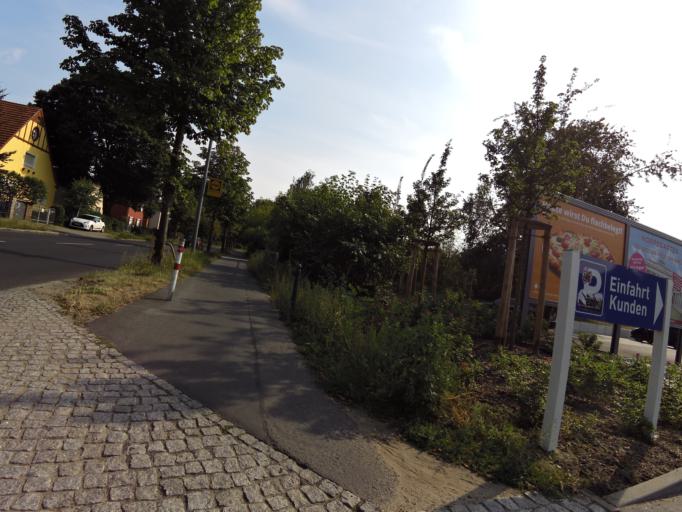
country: DE
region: Berlin
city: Grunau
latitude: 52.4091
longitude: 13.5733
